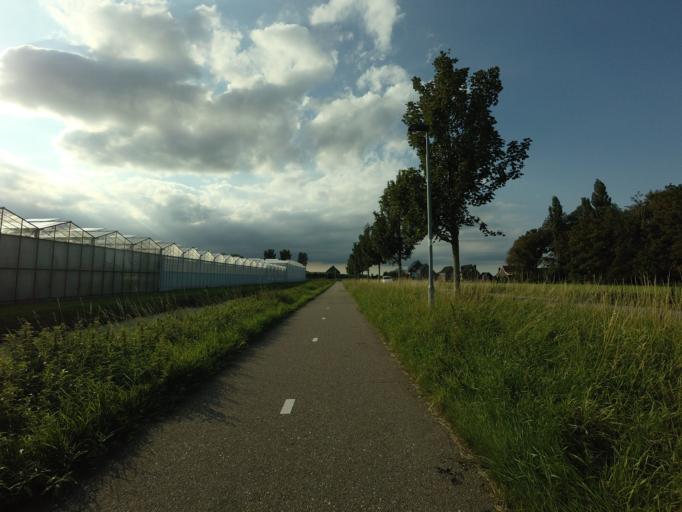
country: NL
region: North Holland
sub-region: Gemeente Hoorn
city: Hoorn
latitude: 52.6913
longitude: 5.0740
